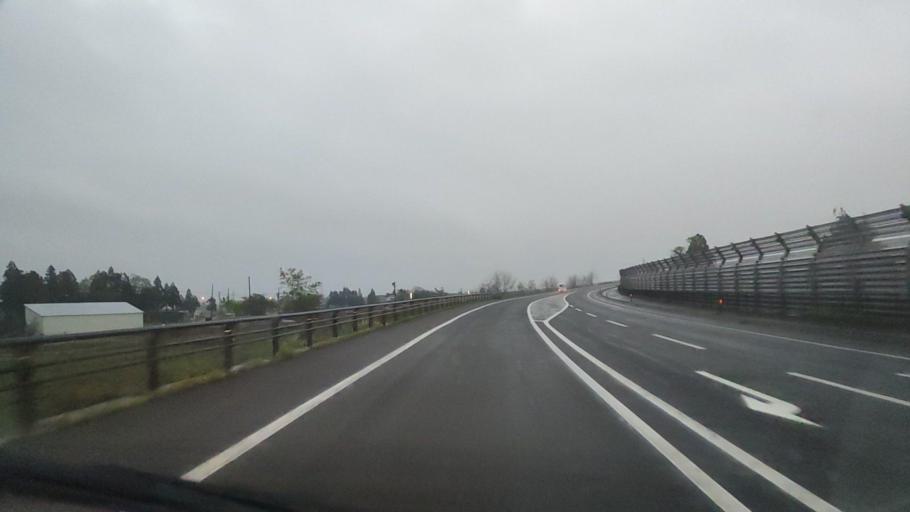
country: JP
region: Akita
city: Omagari
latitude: 39.4957
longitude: 140.4481
